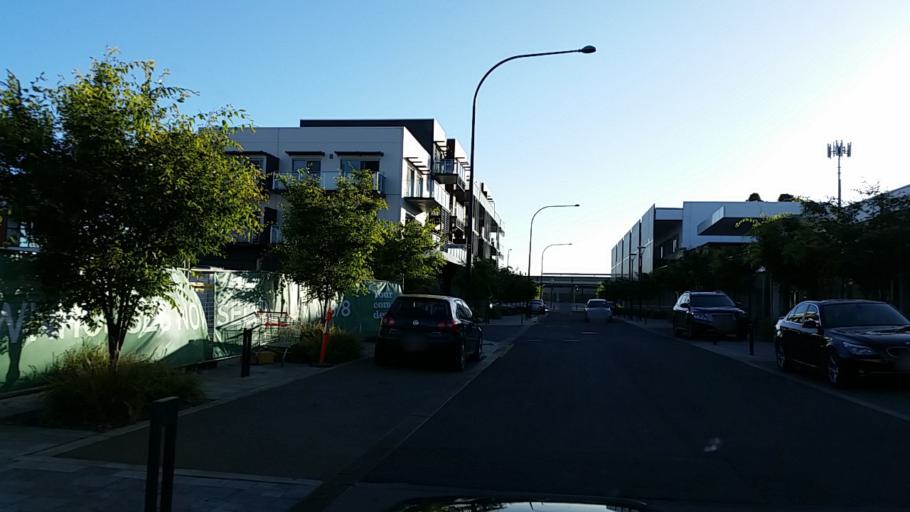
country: AU
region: South Australia
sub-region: Charles Sturt
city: Albert Park
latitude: -34.8696
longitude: 138.5308
